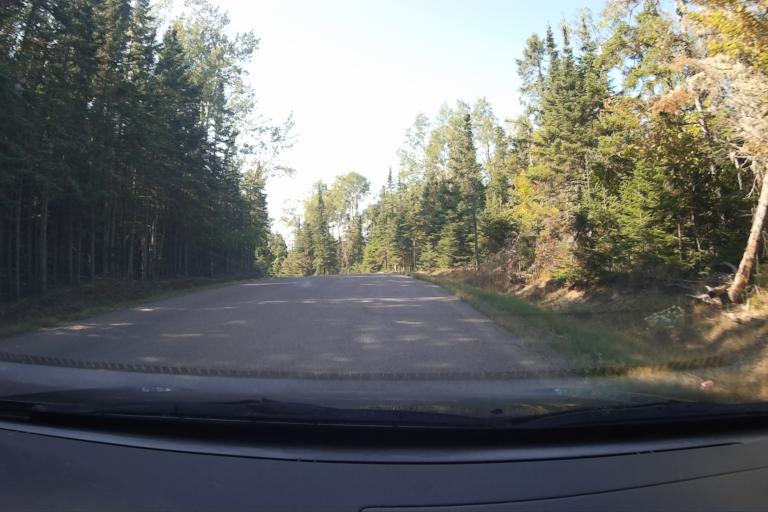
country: CA
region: Ontario
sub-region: Thunder Bay District
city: Thunder Bay
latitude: 48.3398
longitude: -88.8225
